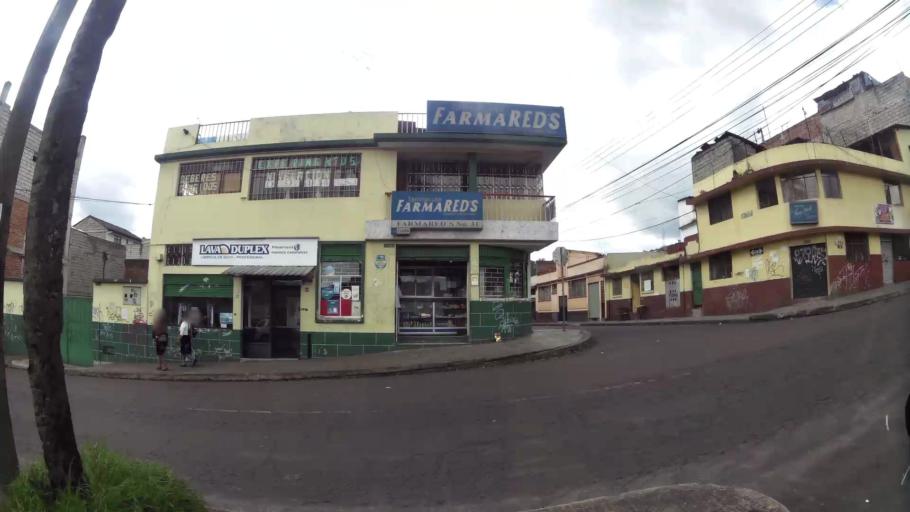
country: EC
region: Pichincha
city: Quito
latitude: -0.2455
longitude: -78.5137
